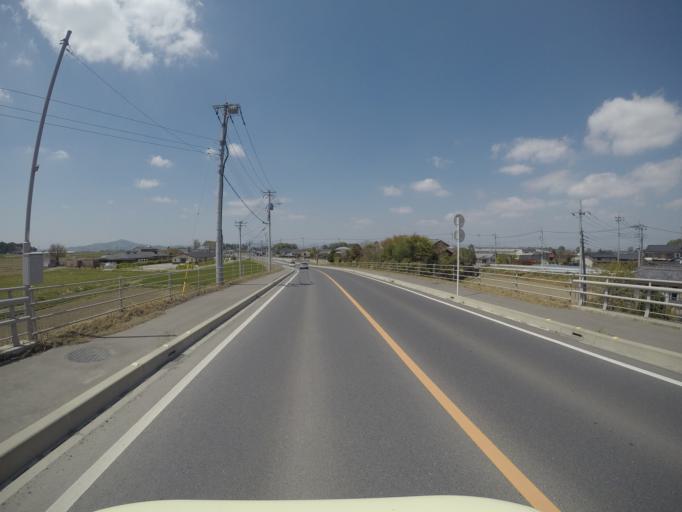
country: JP
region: Tochigi
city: Mibu
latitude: 36.3907
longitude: 139.7930
